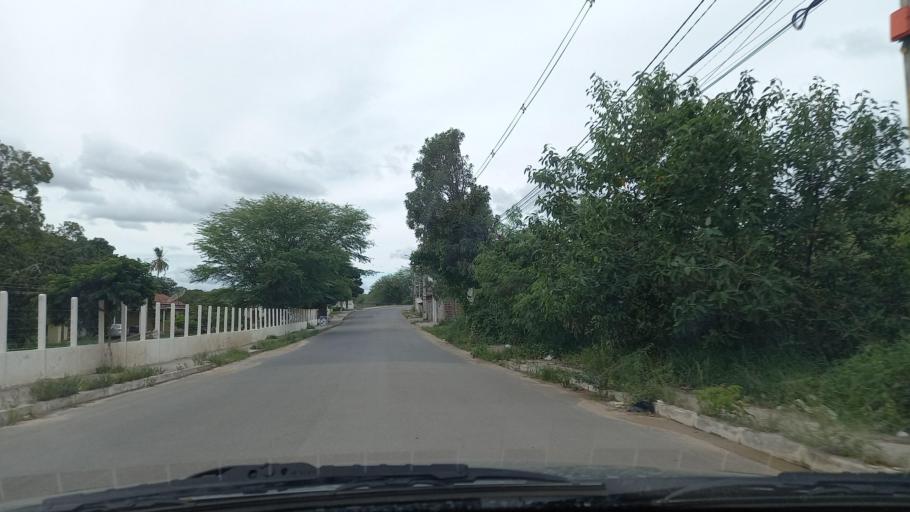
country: BR
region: Pernambuco
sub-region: Gravata
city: Gravata
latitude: -8.2107
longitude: -35.5981
